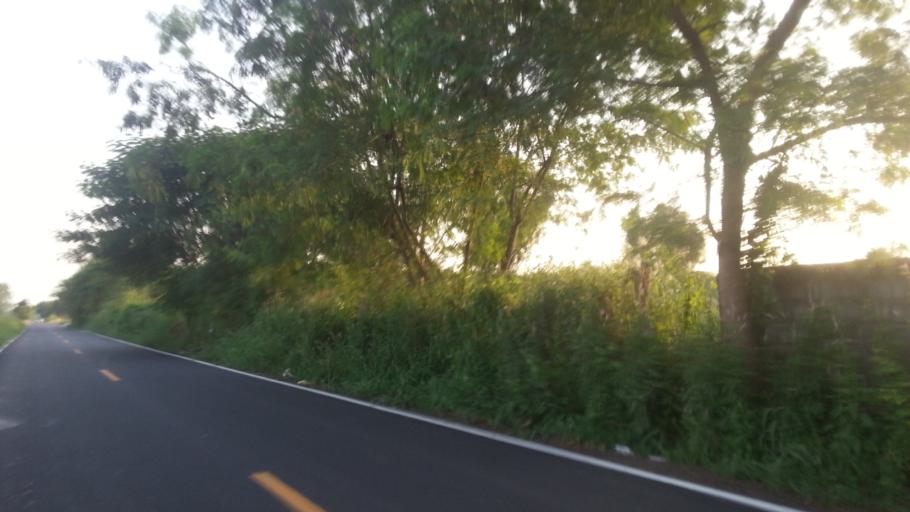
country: TH
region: Pathum Thani
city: Nong Suea
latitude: 14.0462
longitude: 100.8572
